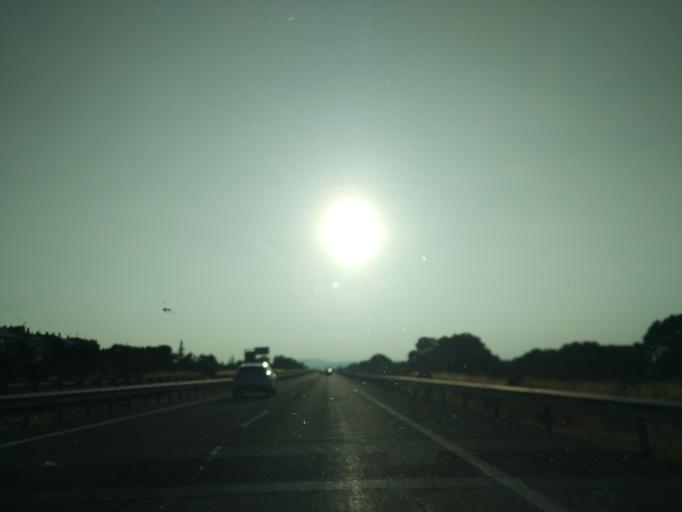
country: ES
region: Castille and Leon
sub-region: Provincia de Avila
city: Avila
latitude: 40.6708
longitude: -4.6608
